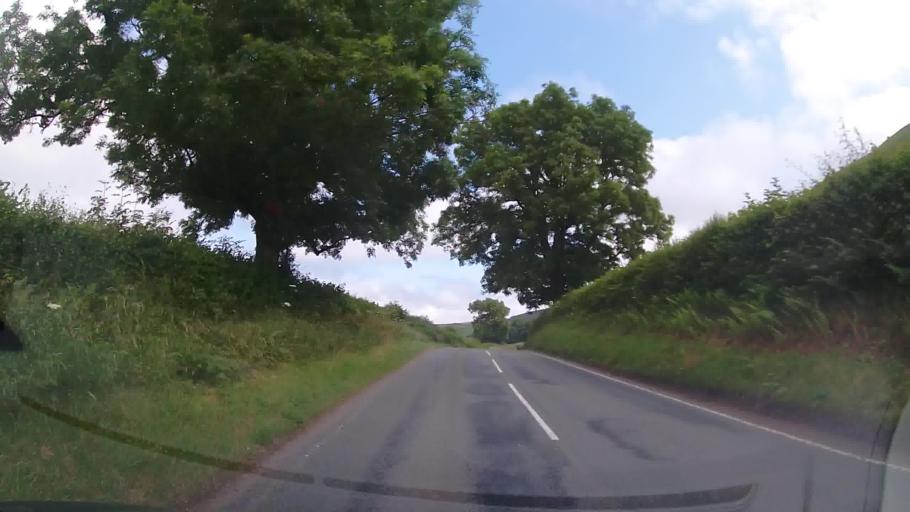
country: GB
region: Wales
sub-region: Sir Powys
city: Llangynog
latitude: 52.8193
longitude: -3.3765
